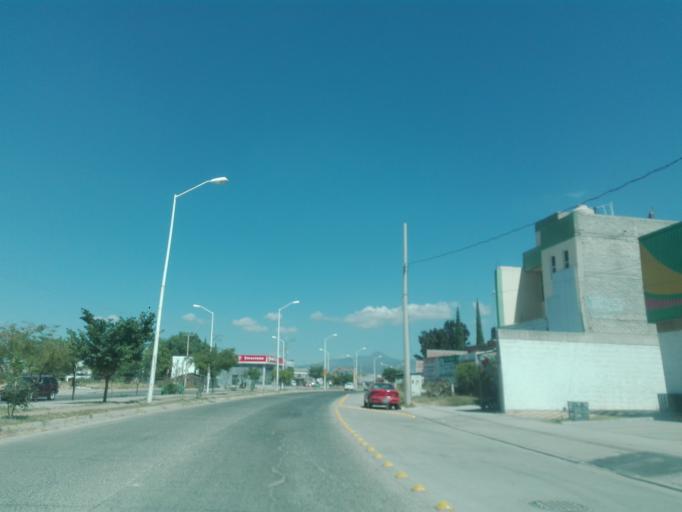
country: MX
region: Guanajuato
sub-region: Leon
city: San Jose de Duran (Los Troncoso)
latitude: 21.0749
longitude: -101.6362
